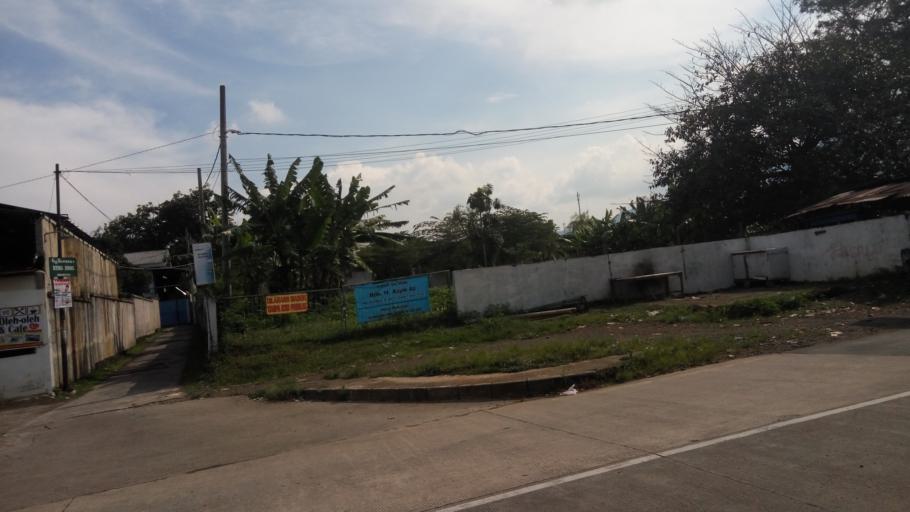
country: ID
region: Central Java
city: Ungaran
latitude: -7.1359
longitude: 110.4128
